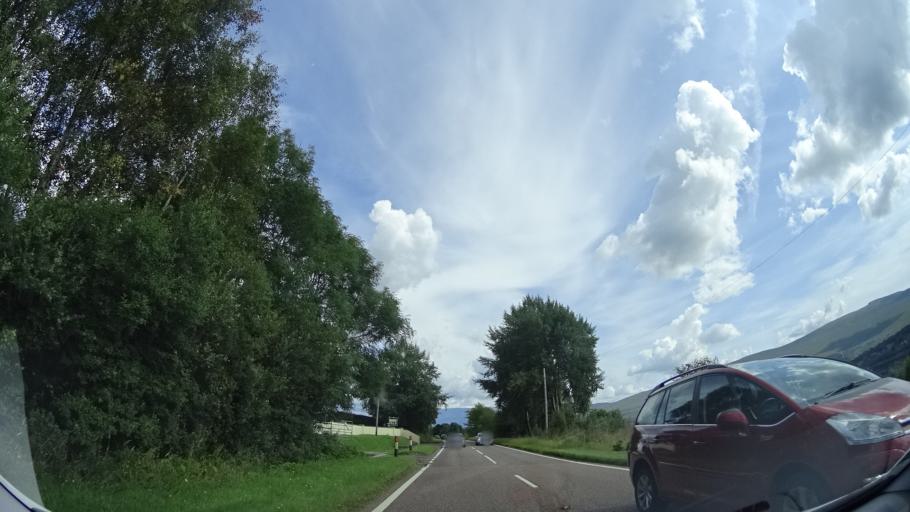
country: GB
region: Scotland
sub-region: Highland
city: Fort William
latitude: 56.8558
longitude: -5.2864
